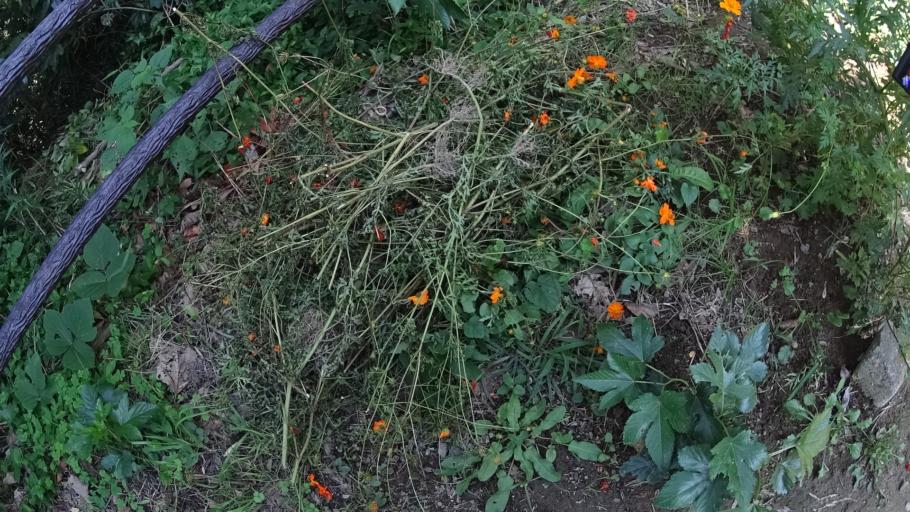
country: JP
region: Kanagawa
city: Kamakura
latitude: 35.3564
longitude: 139.5886
